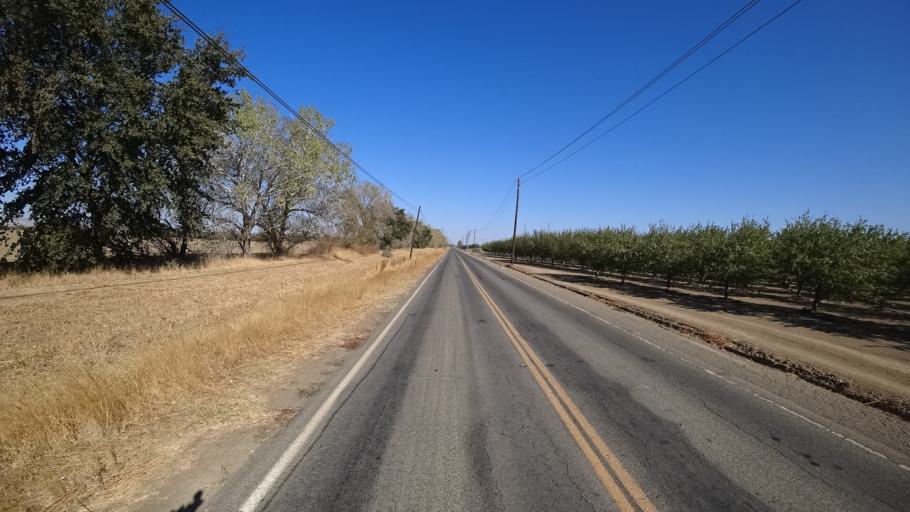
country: US
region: California
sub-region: Yolo County
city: Cottonwood
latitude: 38.6688
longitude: -121.9704
